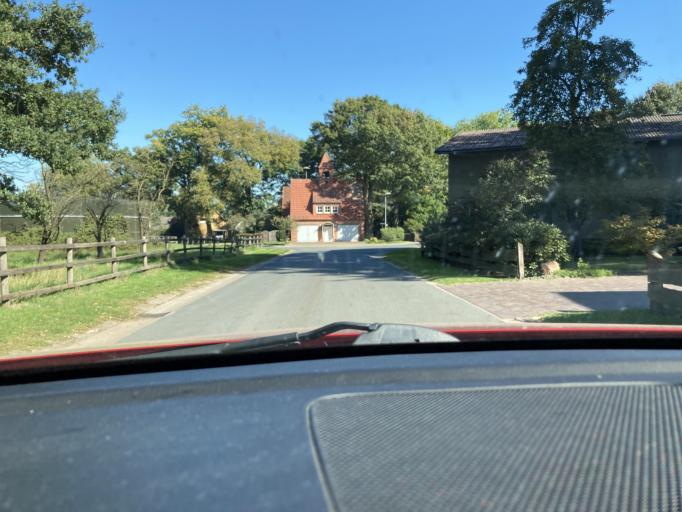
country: DE
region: Lower Saxony
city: Horstedt
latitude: 53.1764
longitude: 9.2314
